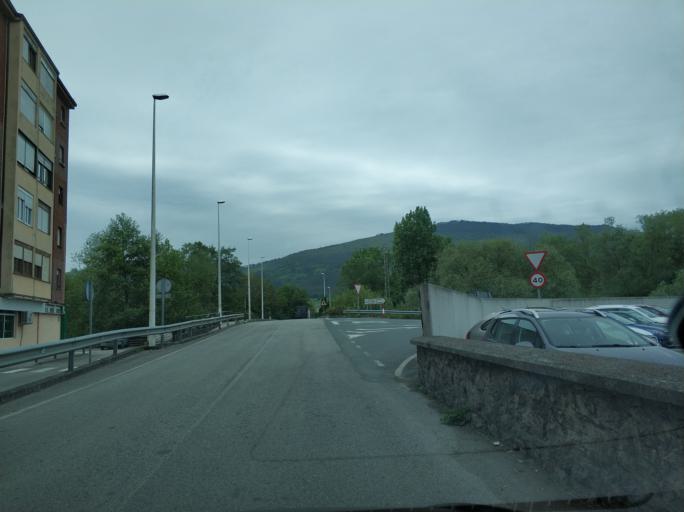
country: ES
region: Cantabria
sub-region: Provincia de Cantabria
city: Santa Maria de Cayon
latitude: 43.3155
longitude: -3.8798
